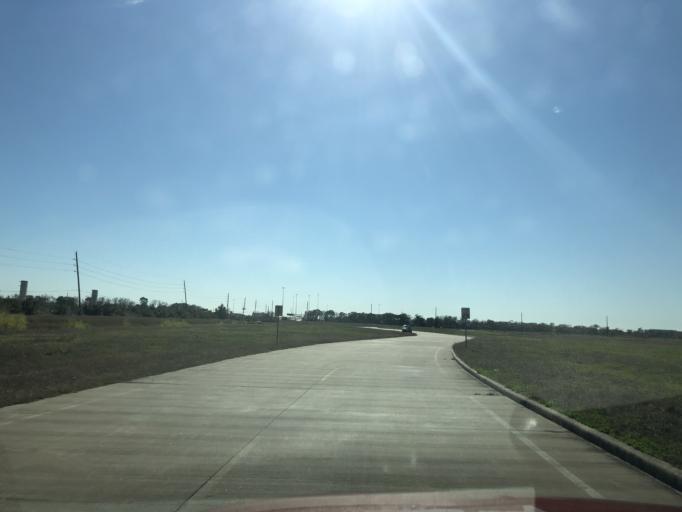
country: US
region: Texas
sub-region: Brazoria County
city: Brookside Village
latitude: 29.5922
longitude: -95.3878
